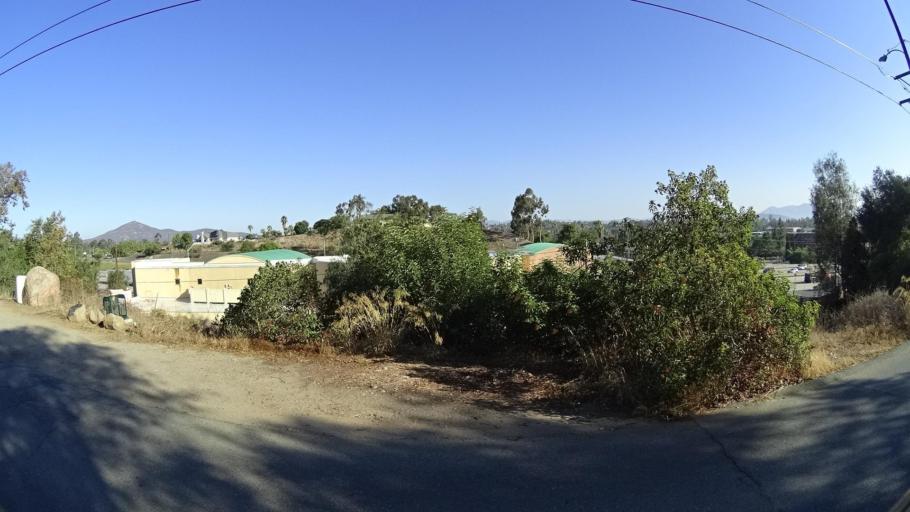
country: US
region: California
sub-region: San Diego County
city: Casa de Oro-Mount Helix
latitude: 32.7782
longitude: -116.9943
